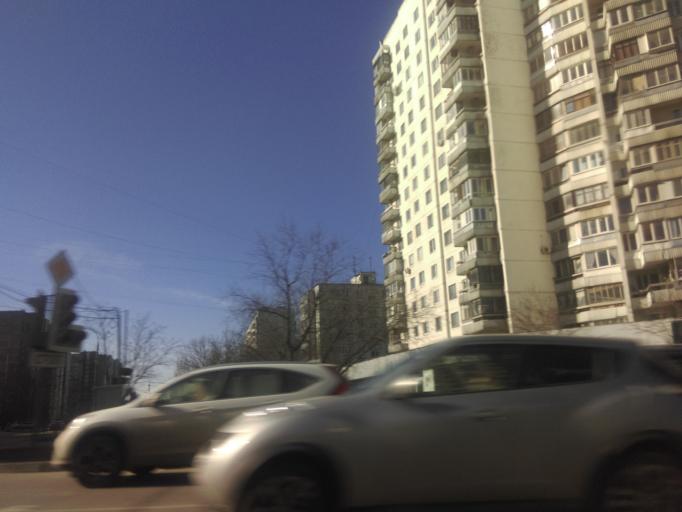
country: RU
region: Moscow
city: Tyoply Stan
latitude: 55.6324
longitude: 37.4808
